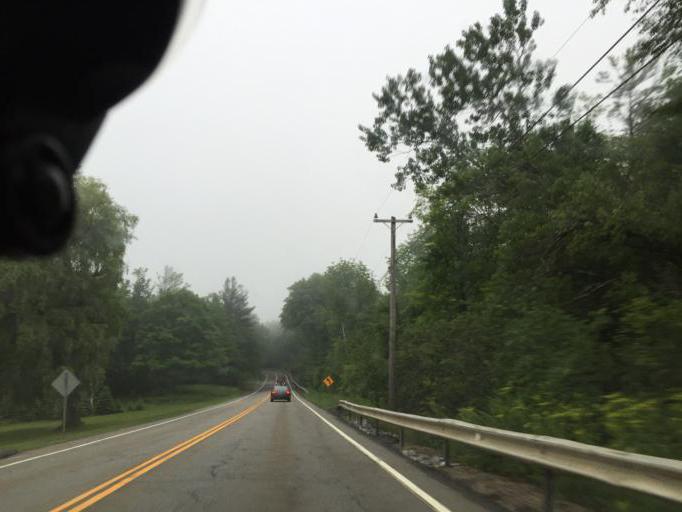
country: US
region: Connecticut
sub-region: Litchfield County
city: Winchester Center
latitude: 41.8888
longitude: -73.2554
